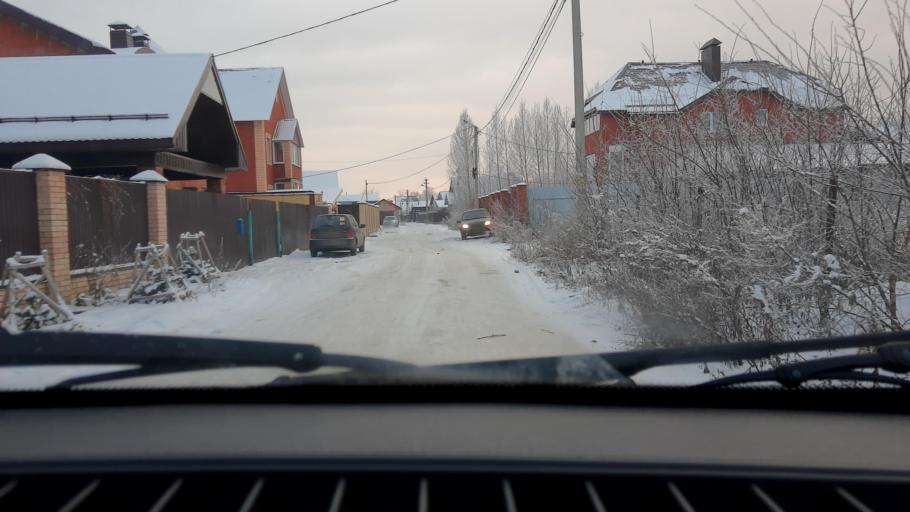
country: RU
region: Bashkortostan
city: Ufa
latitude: 54.6605
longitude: 55.9248
